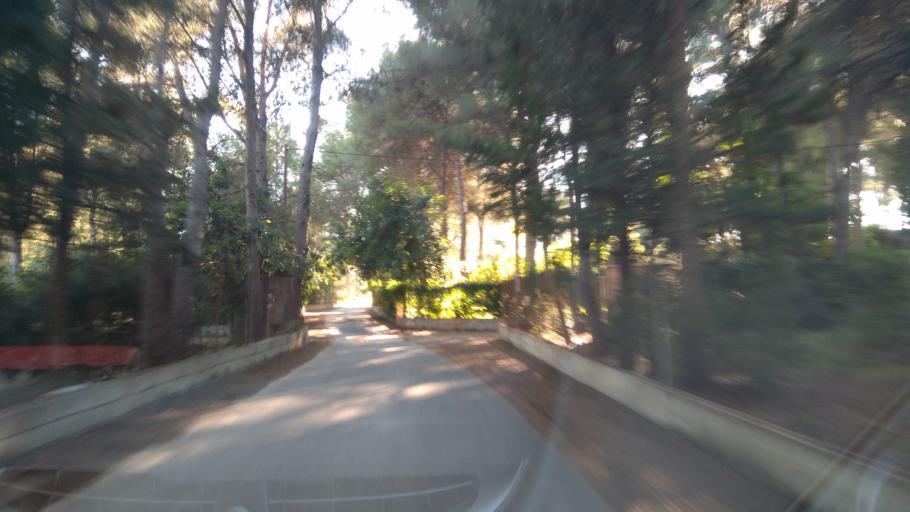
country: ES
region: Valencia
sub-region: Provincia de Valencia
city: Tous
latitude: 39.1765
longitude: -0.5592
